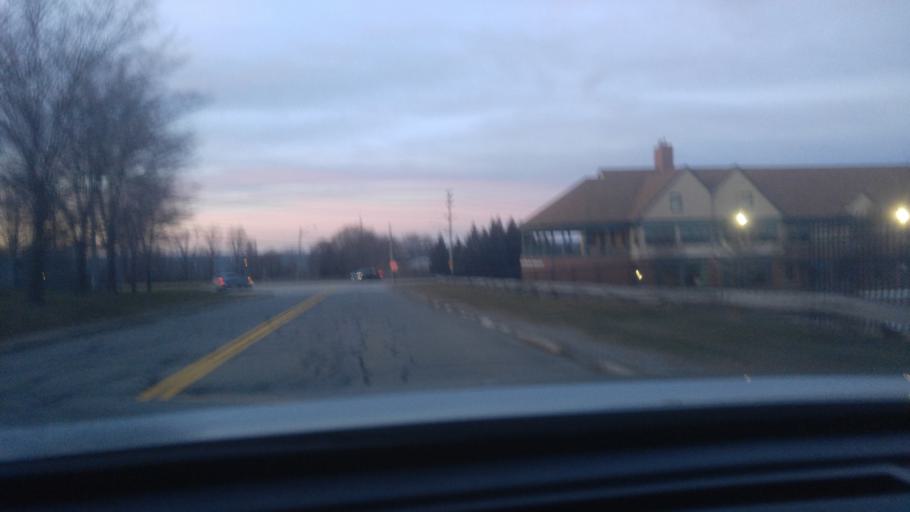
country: US
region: Rhode Island
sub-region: Newport County
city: Newport
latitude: 41.5164
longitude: -71.3143
